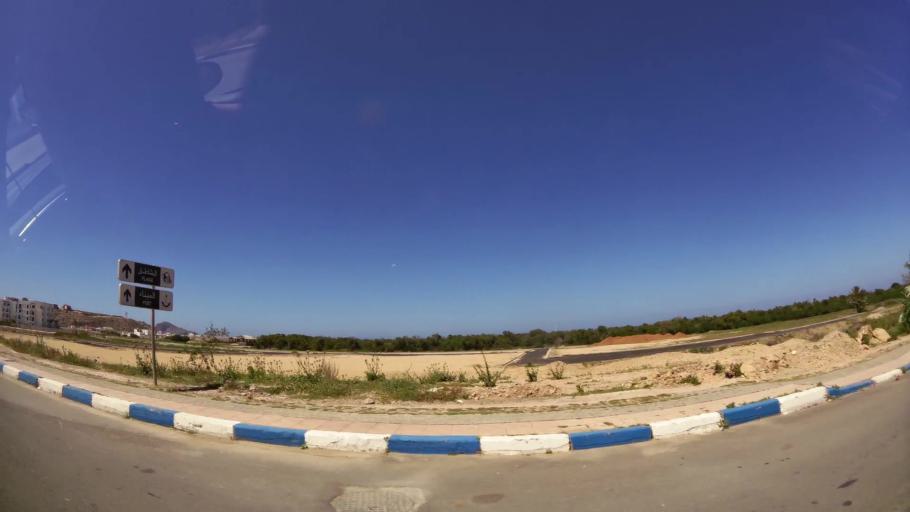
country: MA
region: Oriental
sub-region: Berkane-Taourirt
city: Madagh
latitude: 35.1377
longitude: -2.4180
